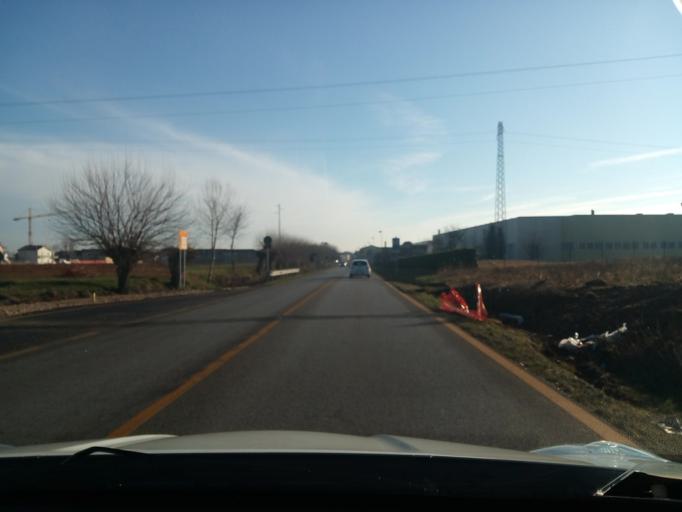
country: IT
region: Veneto
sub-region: Provincia di Vicenza
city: Villaverla
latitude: 45.6620
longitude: 11.4914
